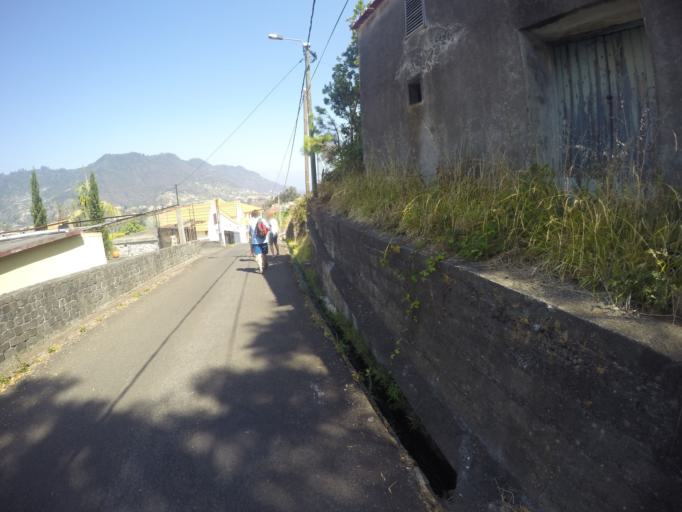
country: PT
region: Madeira
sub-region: Santana
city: Santana
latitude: 32.7582
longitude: -16.8428
